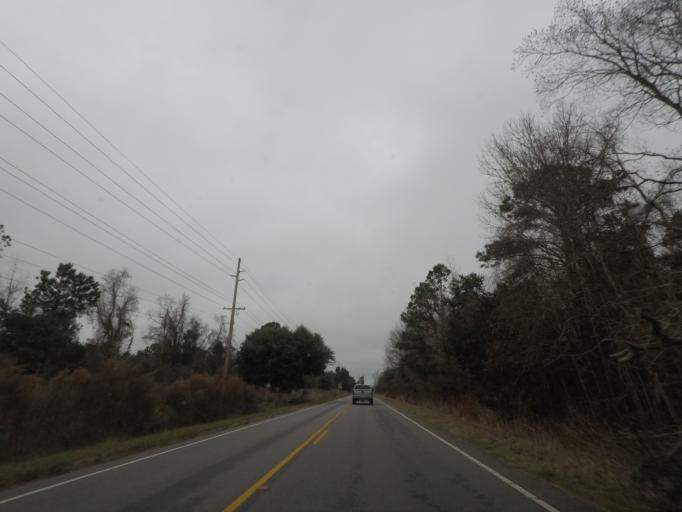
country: US
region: South Carolina
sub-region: Charleston County
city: Meggett
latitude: 32.6208
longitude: -80.3441
